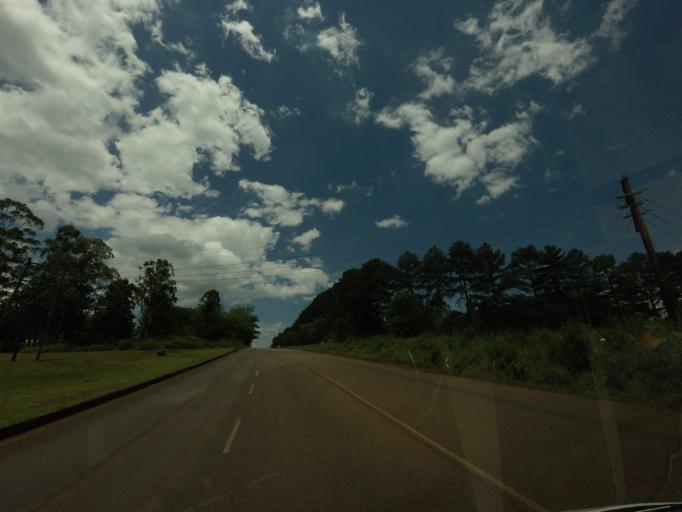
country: ZA
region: Mpumalanga
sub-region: Ehlanzeni District
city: Graksop
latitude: -25.0858
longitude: 30.7843
